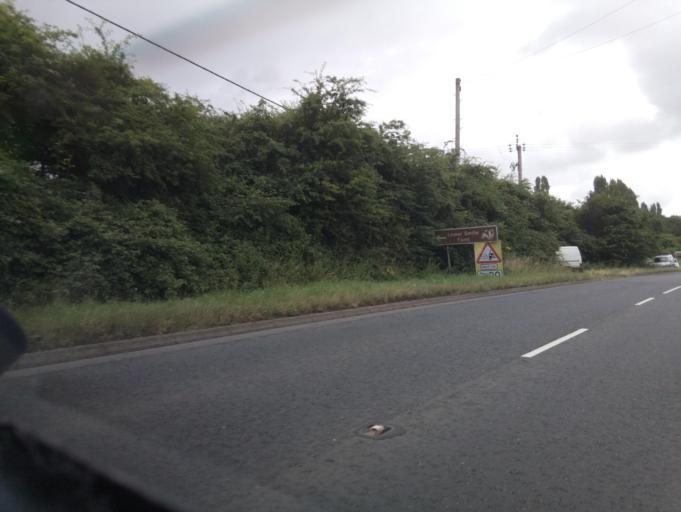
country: GB
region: England
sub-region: Worcestershire
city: Fernhill Heath
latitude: 52.2315
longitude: -2.1704
